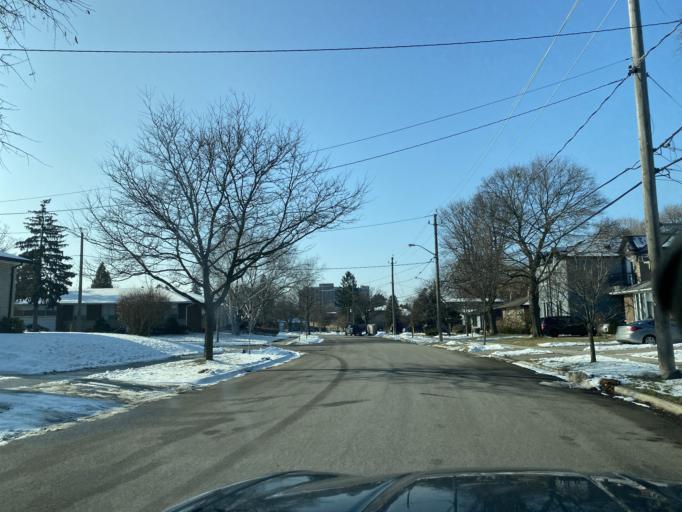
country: CA
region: Ontario
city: Etobicoke
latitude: 43.6588
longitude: -79.5615
